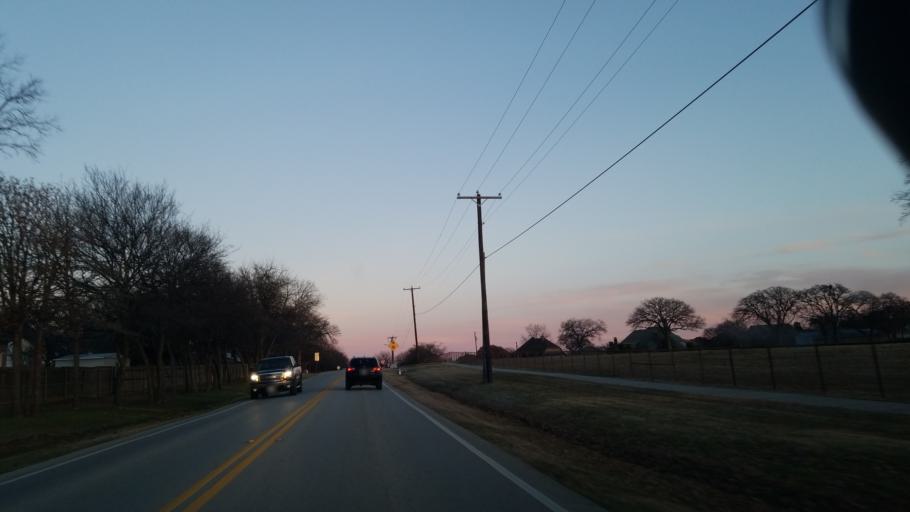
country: US
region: Texas
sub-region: Denton County
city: Denton
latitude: 33.1615
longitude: -97.1325
